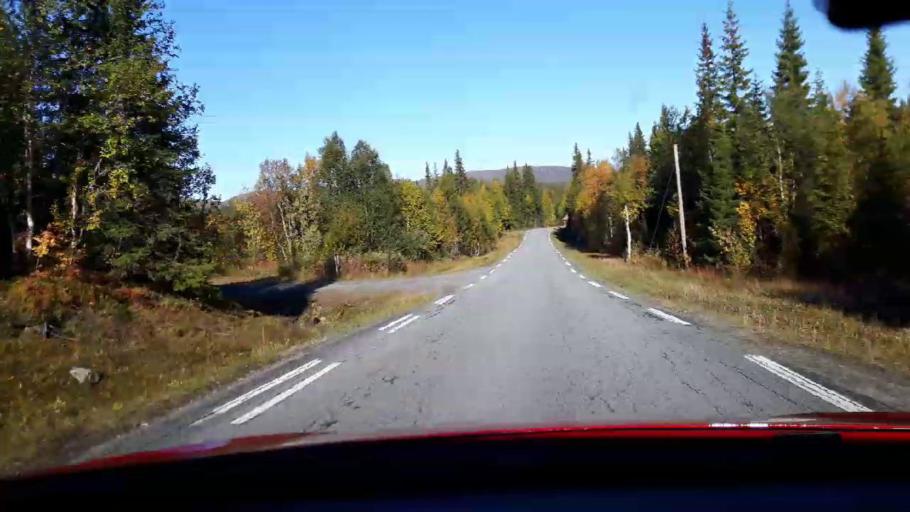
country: NO
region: Nord-Trondelag
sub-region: Lierne
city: Sandvika
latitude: 64.6247
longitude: 13.6864
